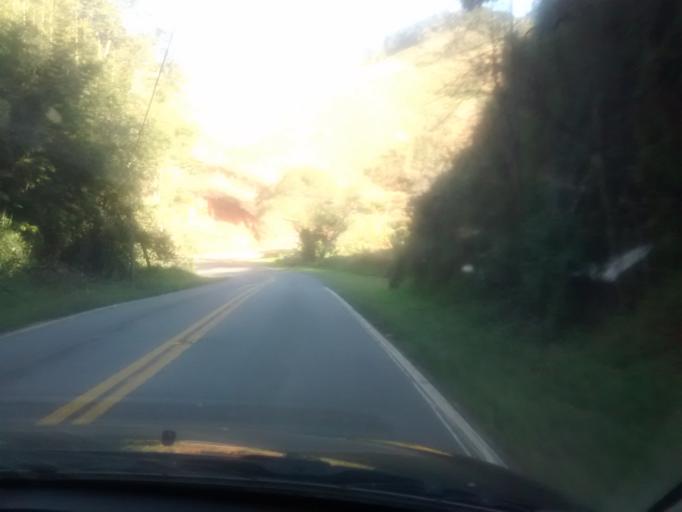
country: BR
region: Sao Paulo
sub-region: Campos Do Jordao
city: Campos do Jordao
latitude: -22.8297
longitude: -45.7100
